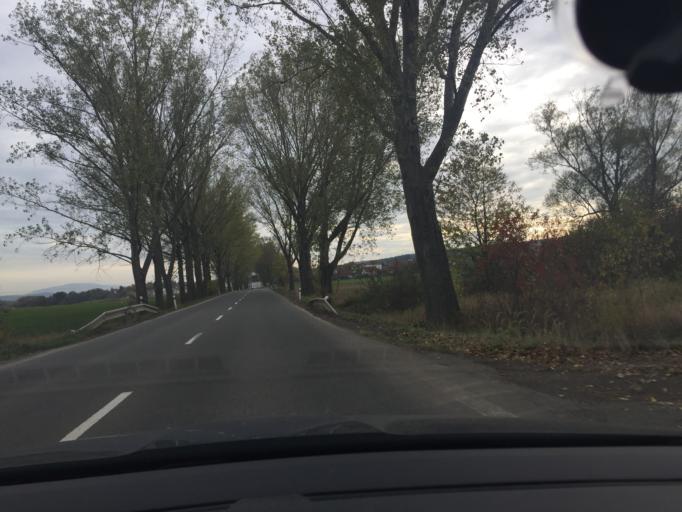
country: SK
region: Kosicky
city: Kosice
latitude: 48.8109
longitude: 21.3006
